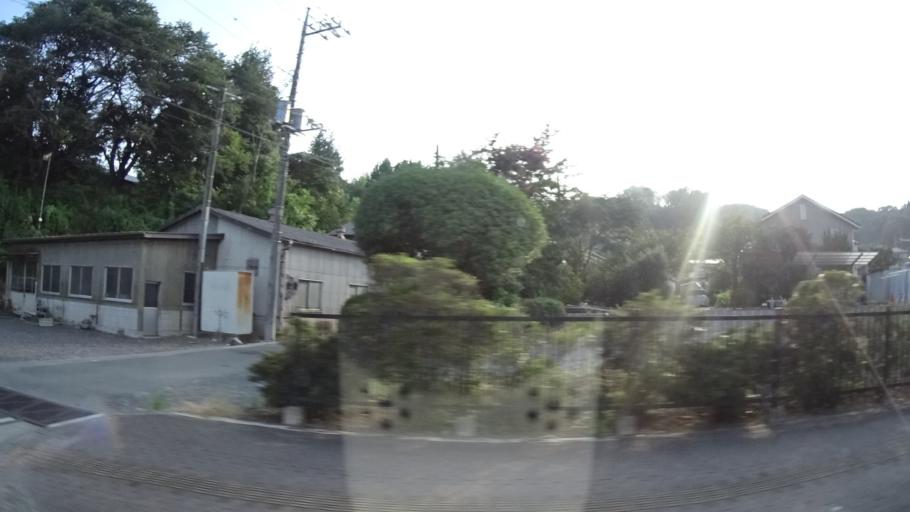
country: JP
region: Tochigi
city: Karasuyama
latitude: 36.6480
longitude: 140.1521
